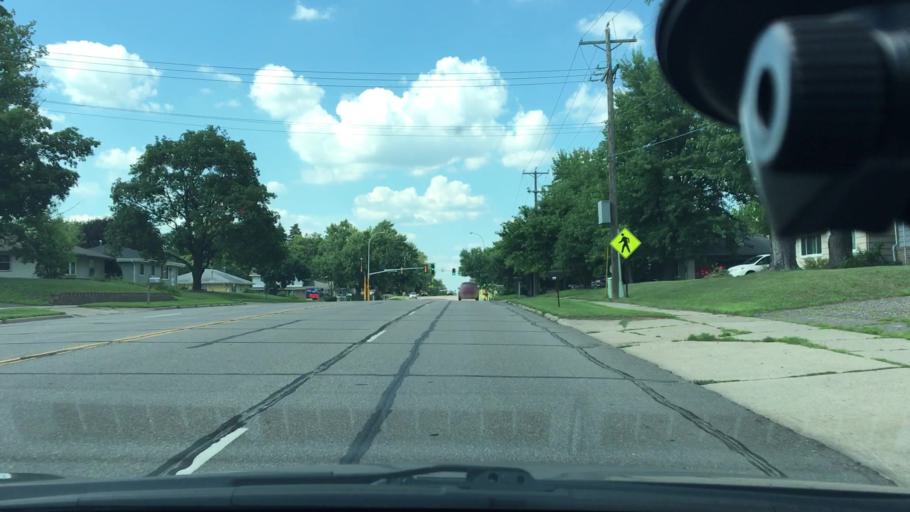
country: US
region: Minnesota
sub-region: Hennepin County
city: New Hope
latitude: 45.0387
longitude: -93.3803
